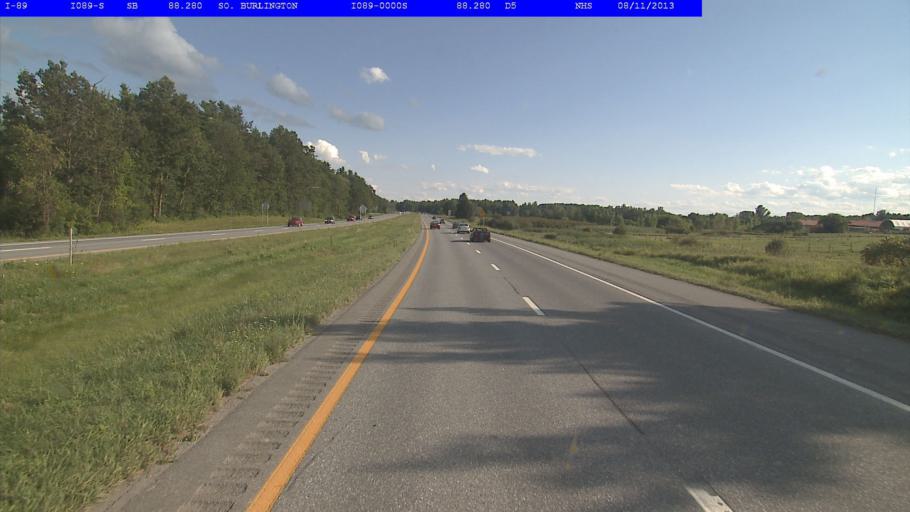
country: US
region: Vermont
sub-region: Chittenden County
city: South Burlington
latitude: 44.4637
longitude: -73.1857
